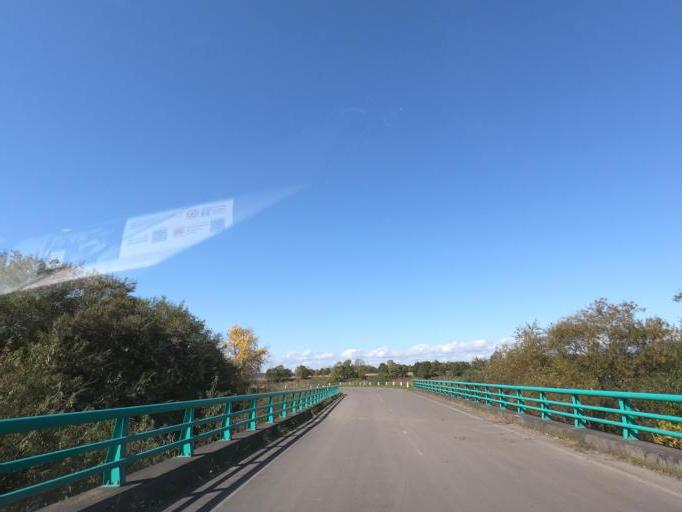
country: JP
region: Hokkaido
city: Otofuke
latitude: 43.0593
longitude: 143.2793
